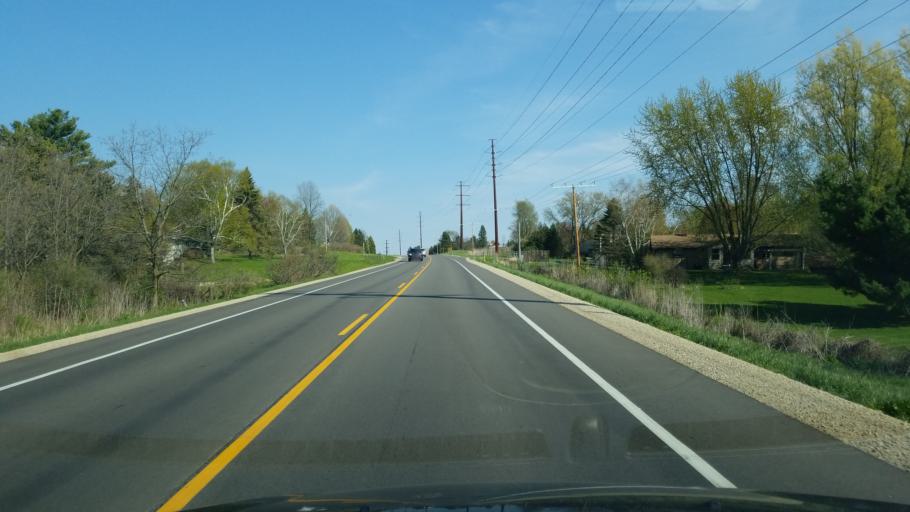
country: US
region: Wisconsin
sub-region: Dane County
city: Fitchburg
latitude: 42.9689
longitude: -89.4966
